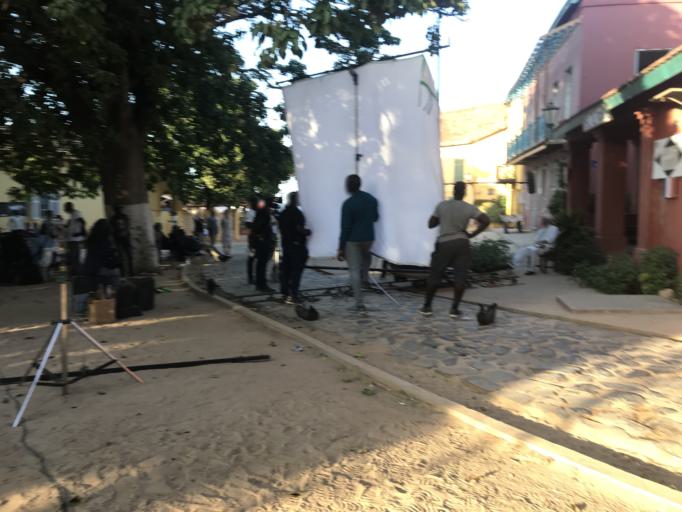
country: SN
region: Dakar
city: Dakar
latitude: 14.6678
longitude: -17.3988
